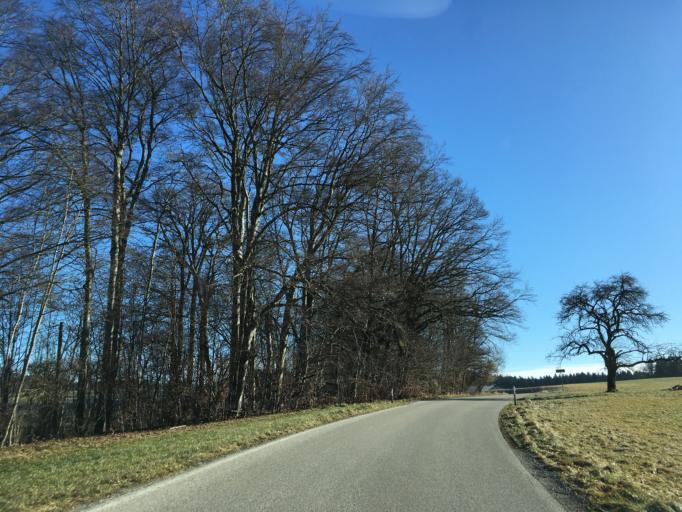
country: DE
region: Bavaria
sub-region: Upper Bavaria
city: Amerang
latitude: 48.0184
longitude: 12.3274
